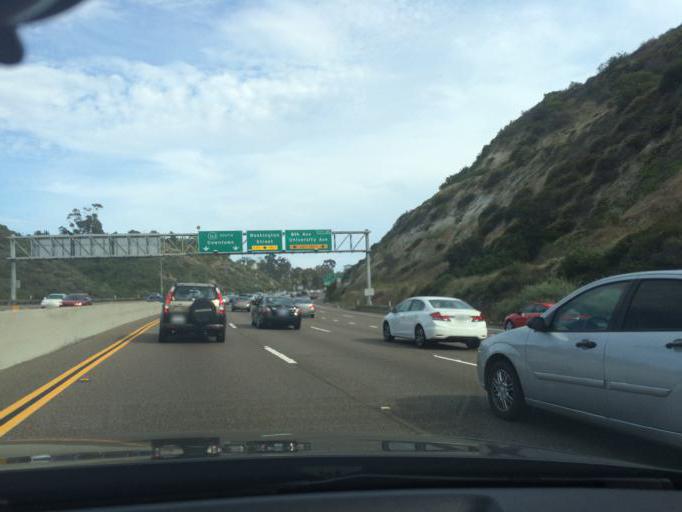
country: US
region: California
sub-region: San Diego County
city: San Diego
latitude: 32.7577
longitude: -117.1601
